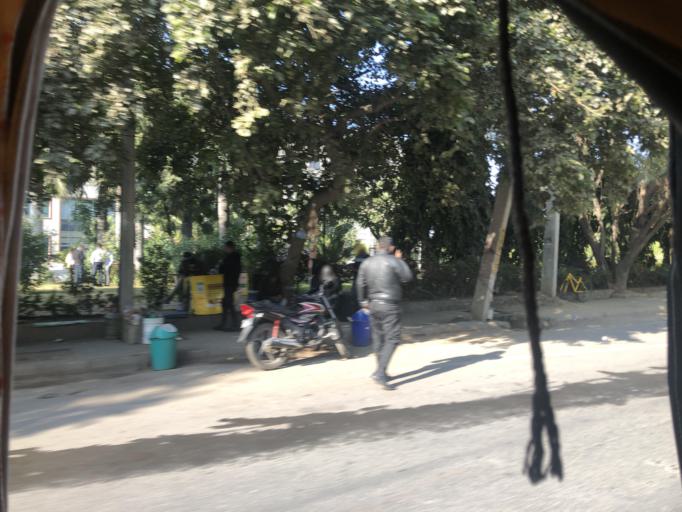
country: IN
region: Haryana
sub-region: Gurgaon
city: Gurgaon
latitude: 28.4616
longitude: 77.0682
